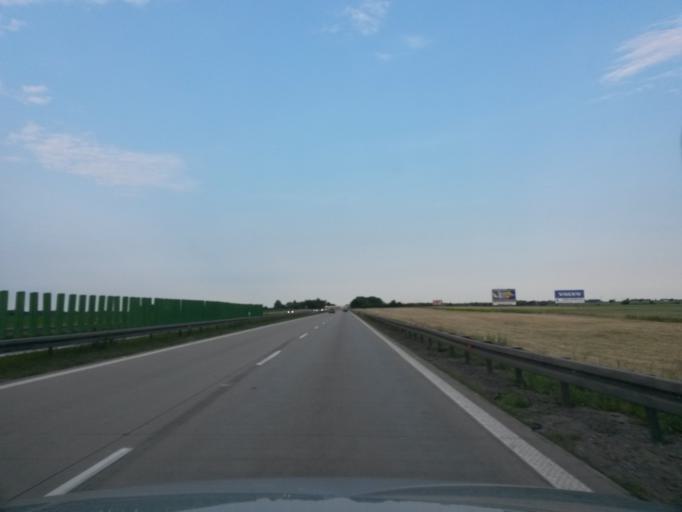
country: PL
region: Lower Silesian Voivodeship
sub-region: Powiat wroclawski
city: Katy Wroclawskie
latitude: 51.0350
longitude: 16.8152
